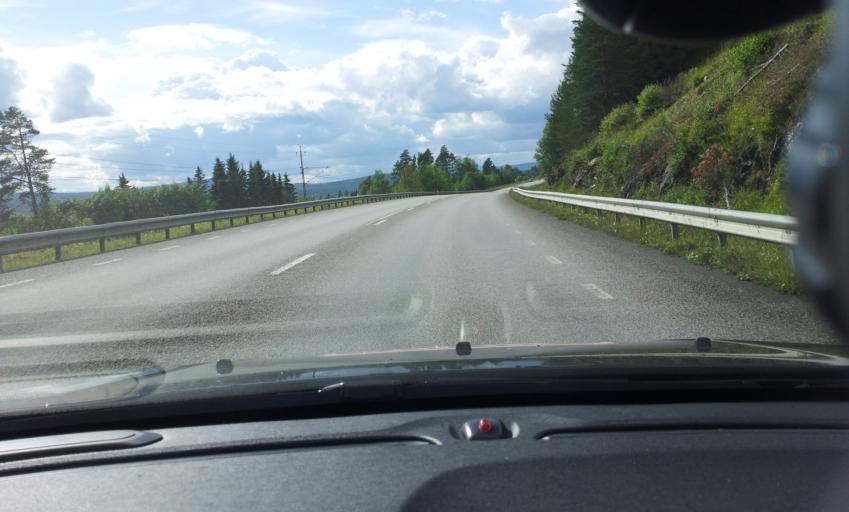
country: SE
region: Jaemtland
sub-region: Are Kommun
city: Jarpen
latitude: 63.3086
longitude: 13.6221
